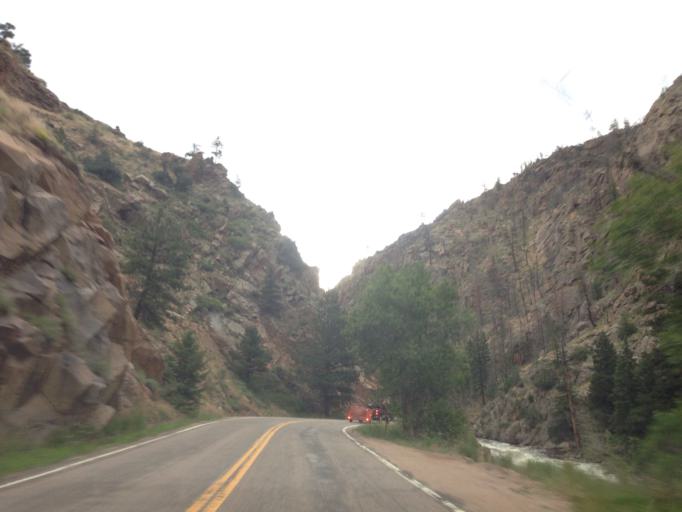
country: US
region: Colorado
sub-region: Larimer County
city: Laporte
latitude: 40.6743
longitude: -105.4176
